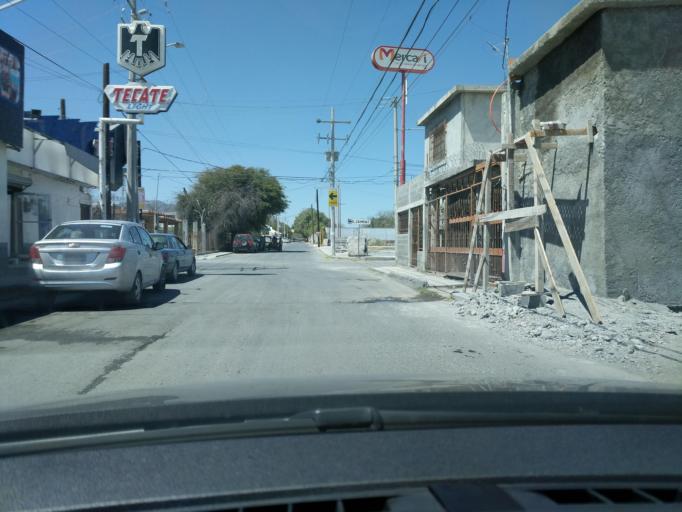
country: MX
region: Nuevo Leon
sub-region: Salinas Victoria
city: Las Torres
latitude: 25.9651
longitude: -100.2954
